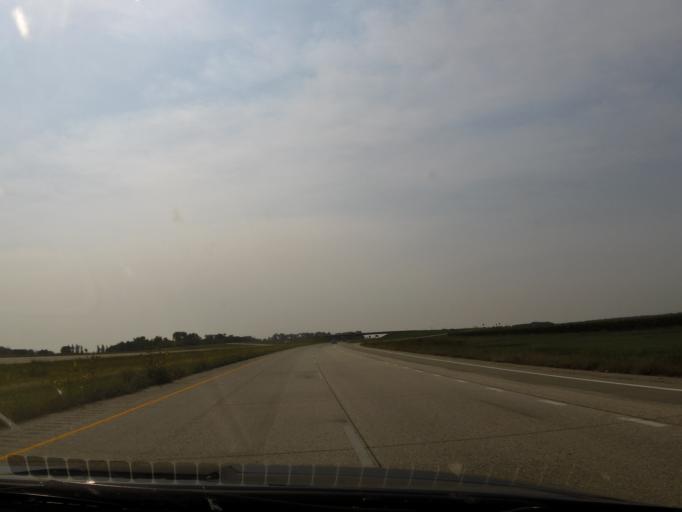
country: US
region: North Dakota
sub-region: Cass County
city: Horace
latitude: 46.7218
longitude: -96.8312
